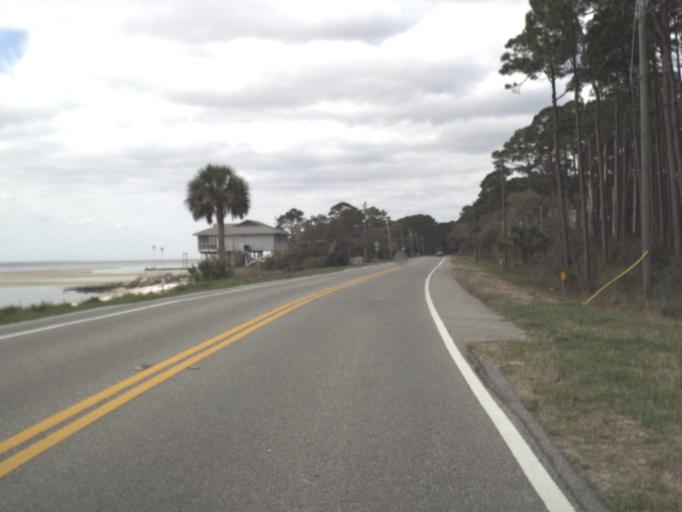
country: US
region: Florida
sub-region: Franklin County
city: Carrabelle
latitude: 29.8128
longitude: -84.7193
